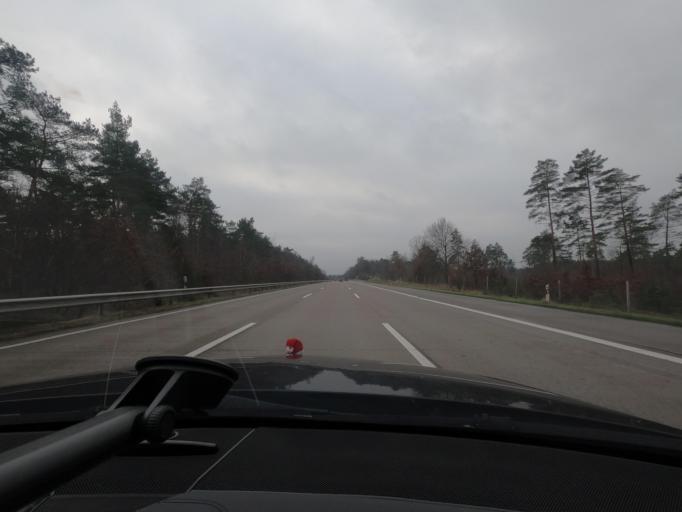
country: DE
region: Lower Saxony
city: Bispingen
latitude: 53.0513
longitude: 9.9521
